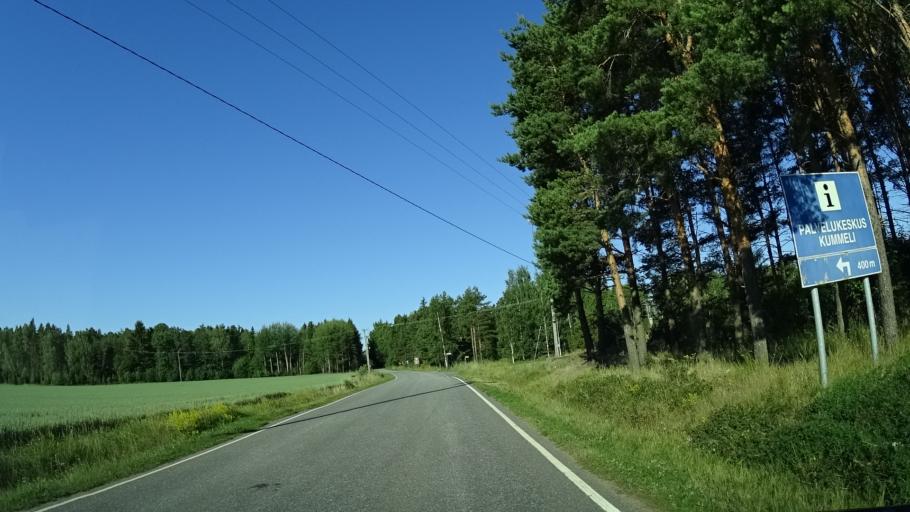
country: FI
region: Varsinais-Suomi
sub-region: Turku
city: Velkua
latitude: 60.4701
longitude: 21.7041
